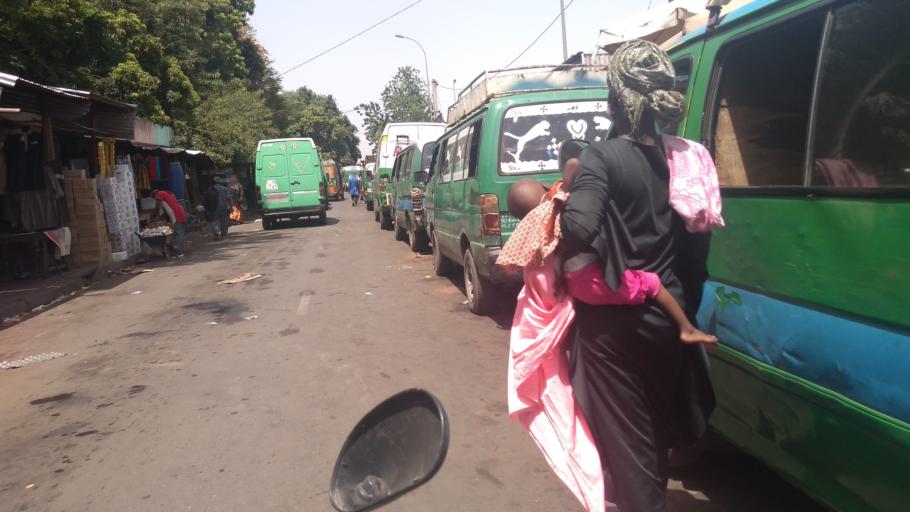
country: ML
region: Bamako
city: Bamako
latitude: 12.6490
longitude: -7.9987
